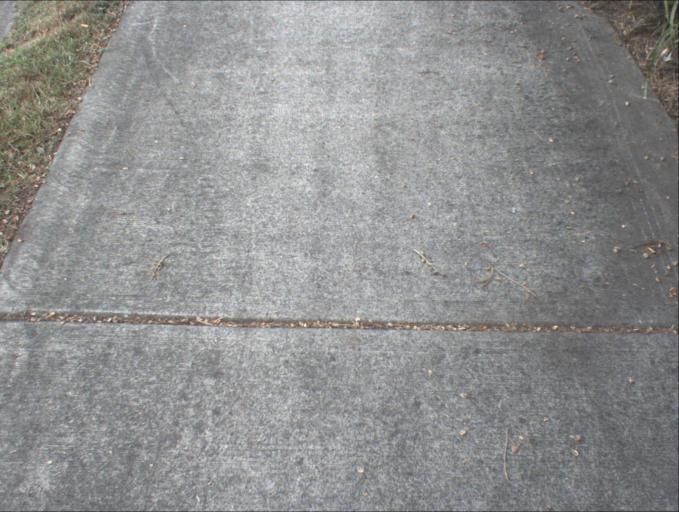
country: AU
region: Queensland
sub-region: Logan
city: Beenleigh
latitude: -27.7128
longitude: 153.1787
